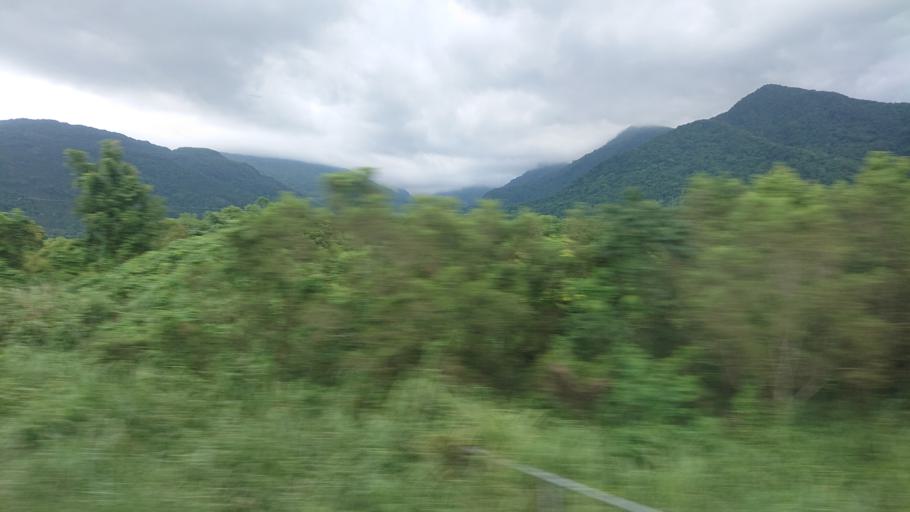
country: TW
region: Taiwan
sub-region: Hualien
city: Hualian
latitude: 23.6096
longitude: 121.3901
